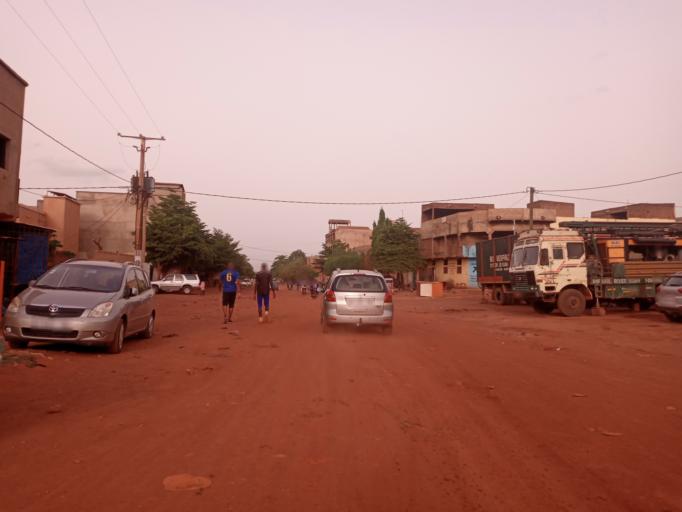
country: ML
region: Bamako
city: Bamako
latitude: 12.5579
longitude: -7.9833
